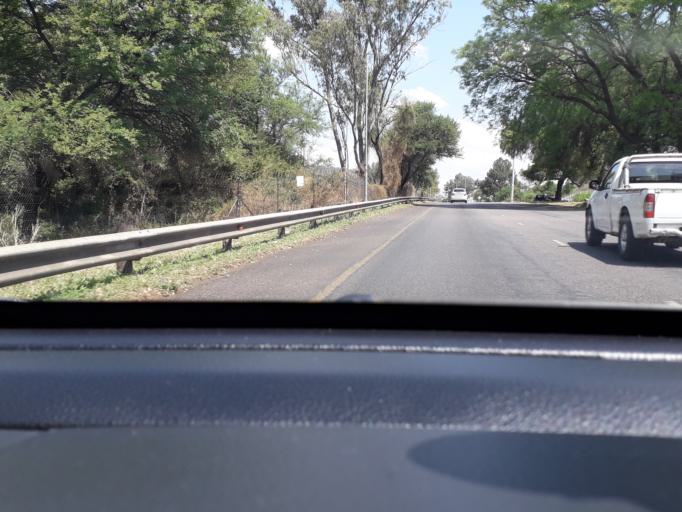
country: ZA
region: Gauteng
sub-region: City of Tshwane Metropolitan Municipality
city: Pretoria
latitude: -25.7832
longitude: 28.1937
